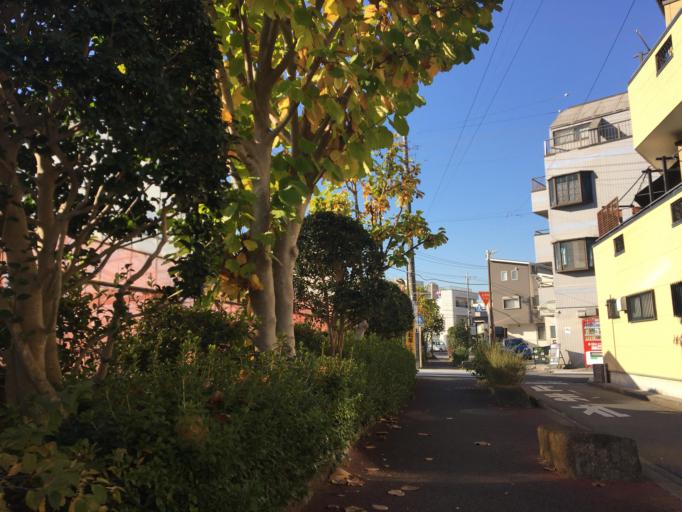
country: JP
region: Tokyo
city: Urayasu
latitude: 35.7172
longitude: 139.8925
